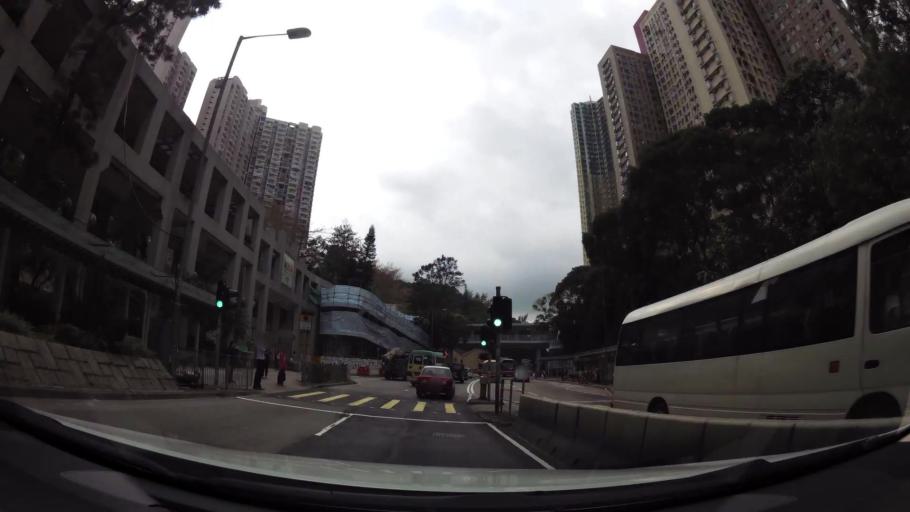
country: HK
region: Wong Tai Sin
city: Wong Tai Sin
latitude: 22.3430
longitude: 114.2004
